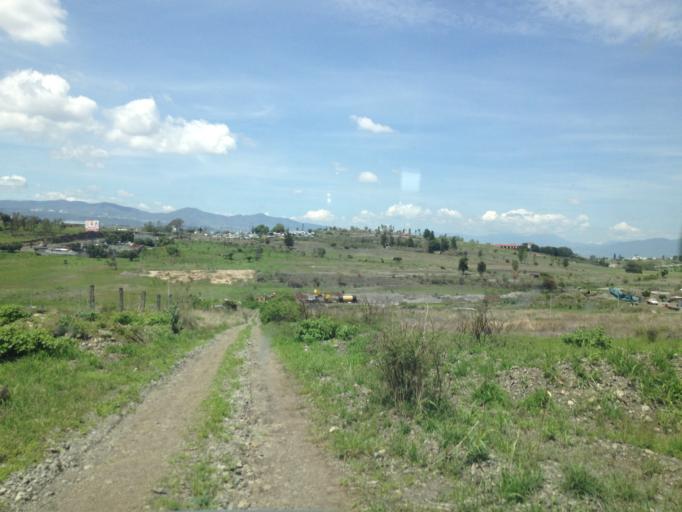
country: MX
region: Michoacan
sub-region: Tarimbaro
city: San Bernabe de las Canteras
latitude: 19.7672
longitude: -101.1660
